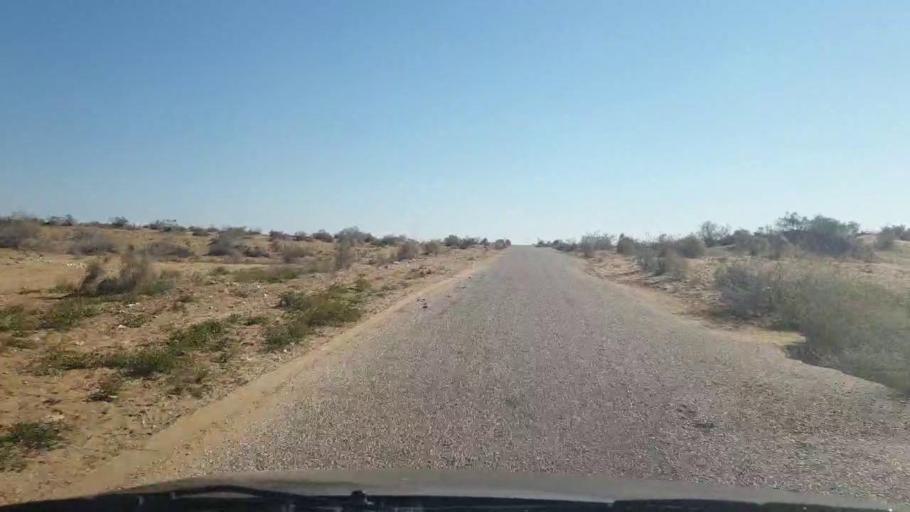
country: PK
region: Sindh
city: Bozdar
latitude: 27.0027
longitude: 68.8067
